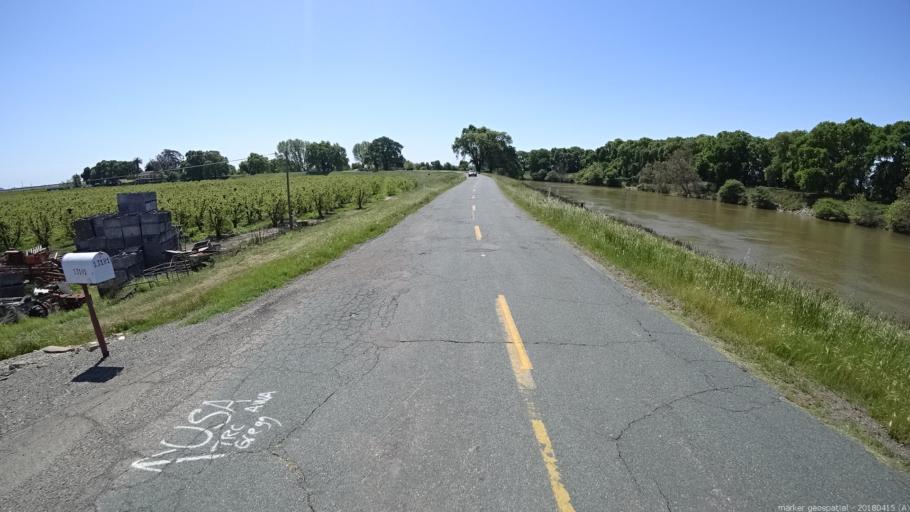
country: US
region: California
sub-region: Sacramento County
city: Walnut Grove
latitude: 38.2779
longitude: -121.5891
